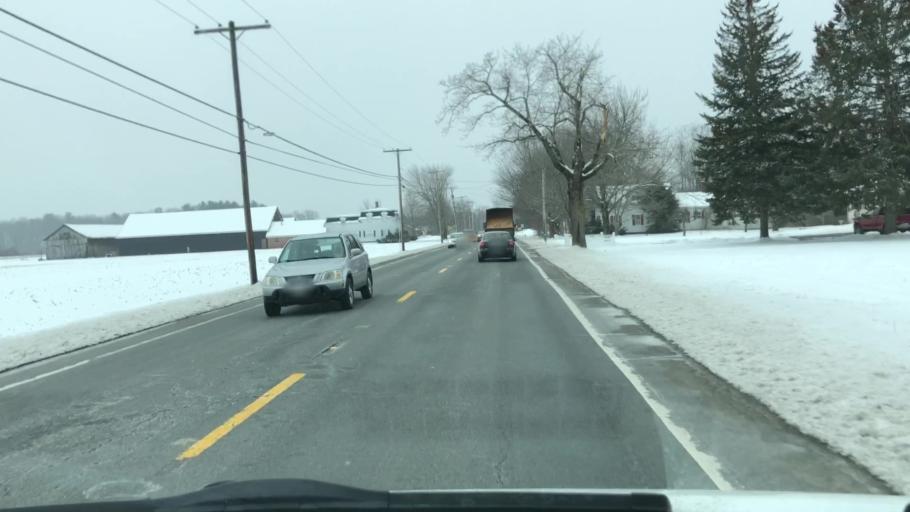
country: US
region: Massachusetts
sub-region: Franklin County
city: Whately
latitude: 42.4052
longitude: -72.6245
